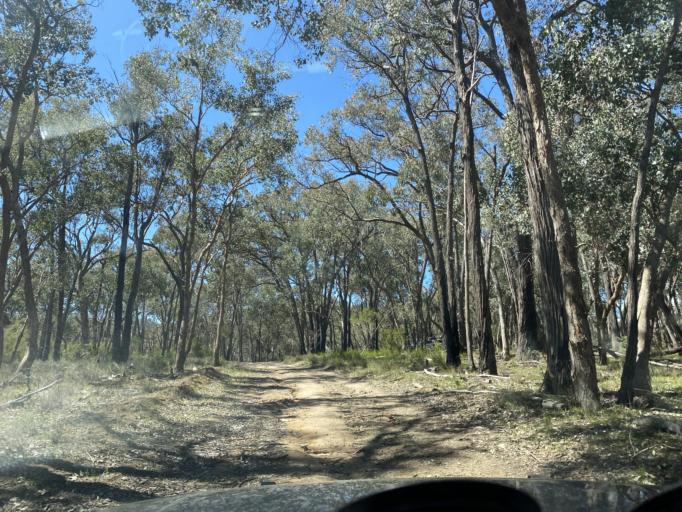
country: AU
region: Victoria
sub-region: Benalla
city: Benalla
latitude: -36.7041
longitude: 146.1533
